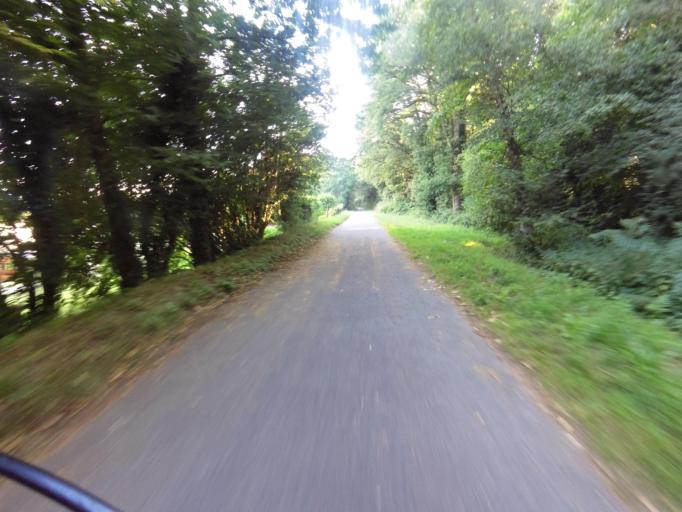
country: FR
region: Brittany
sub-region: Departement du Morbihan
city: Guillac
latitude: 47.9053
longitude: -2.4323
